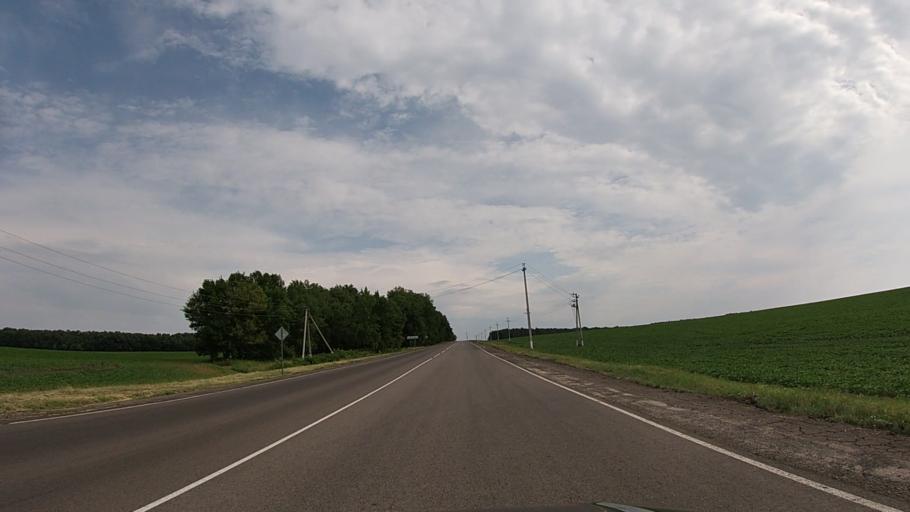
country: RU
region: Belgorod
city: Krasnaya Yaruga
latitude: 50.8094
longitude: 35.5001
